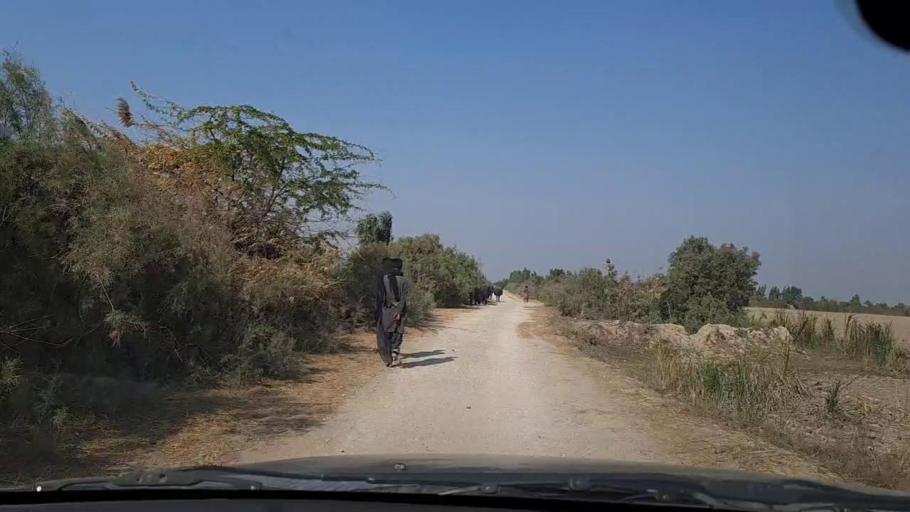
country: PK
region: Sindh
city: Mirpur Sakro
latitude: 24.3481
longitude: 67.6831
